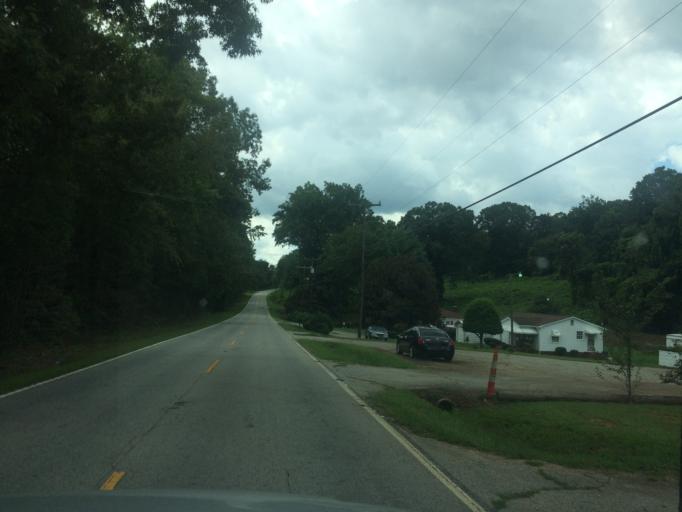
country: US
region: South Carolina
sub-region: Spartanburg County
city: Inman
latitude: 35.1478
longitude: -82.0369
